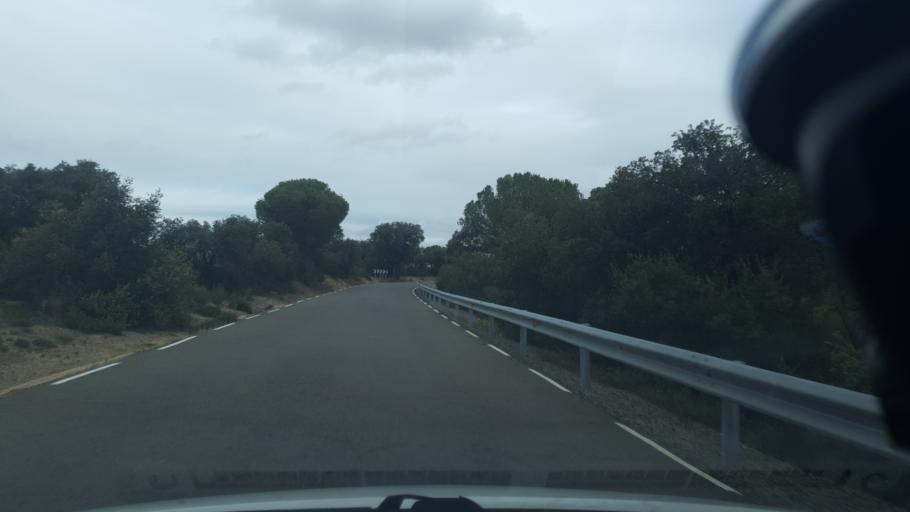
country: ES
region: Castille and Leon
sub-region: Provincia de Avila
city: Pozanco
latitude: 40.8246
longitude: -4.6836
